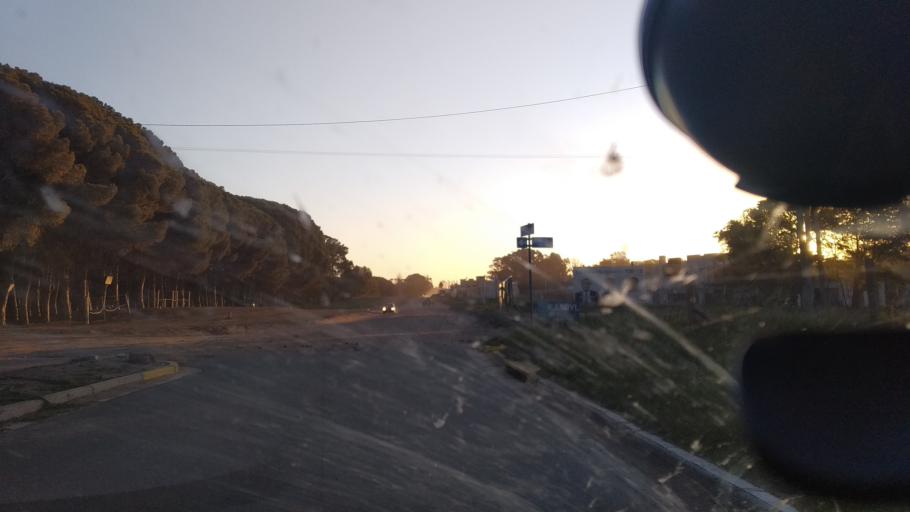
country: AR
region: Buenos Aires
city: Necochea
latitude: -38.5865
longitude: -58.7534
